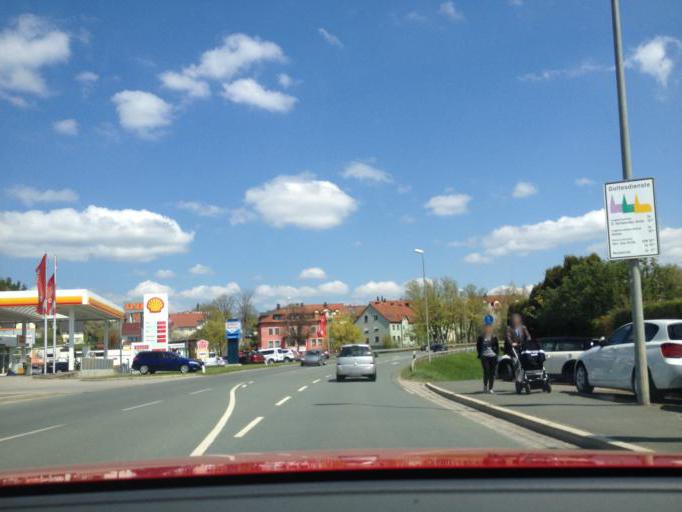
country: DE
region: Bavaria
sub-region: Upper Franconia
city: Pegnitz
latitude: 49.7452
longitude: 11.5346
